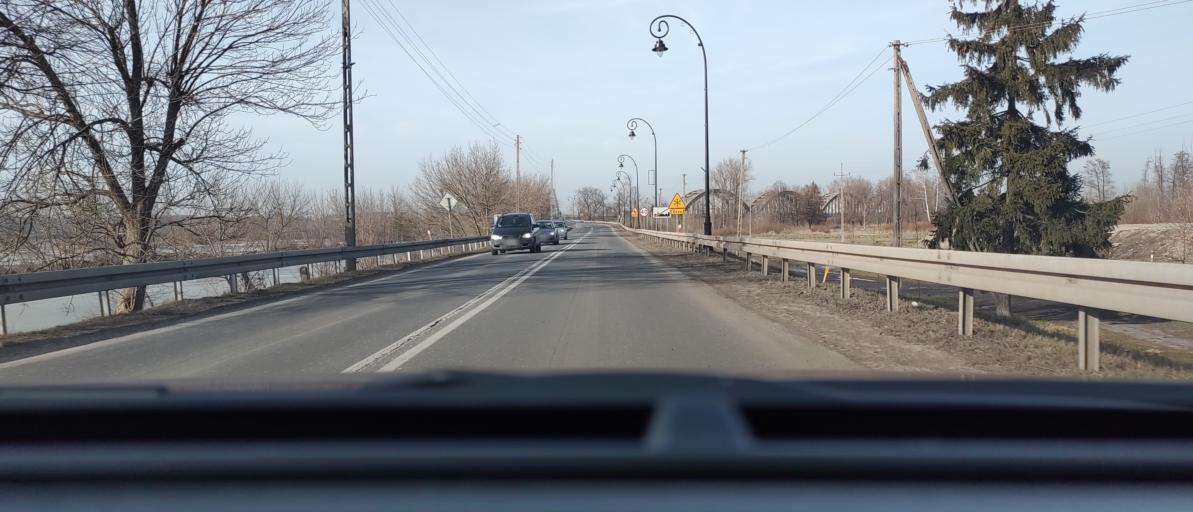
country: PL
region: Masovian Voivodeship
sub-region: Powiat bialobrzeski
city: Bialobrzegi
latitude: 51.6536
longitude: 20.9518
